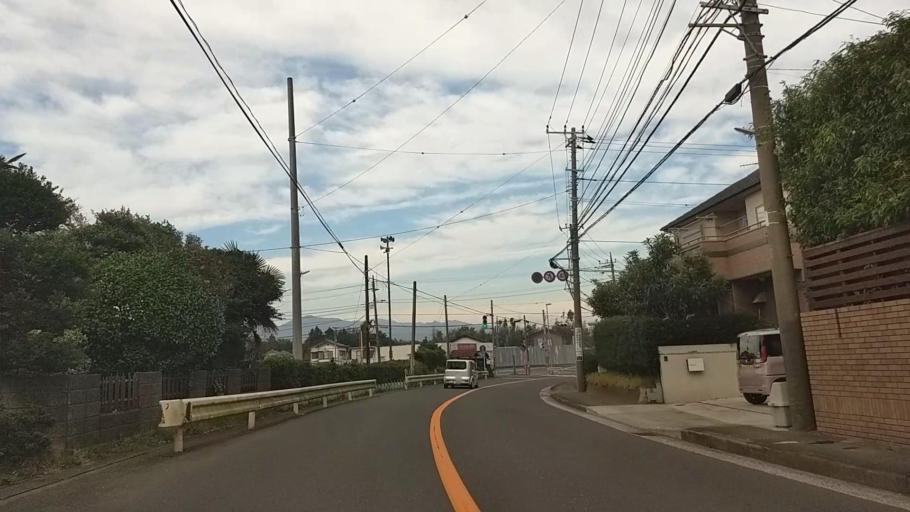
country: JP
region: Kanagawa
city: Atsugi
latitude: 35.4044
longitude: 139.4107
